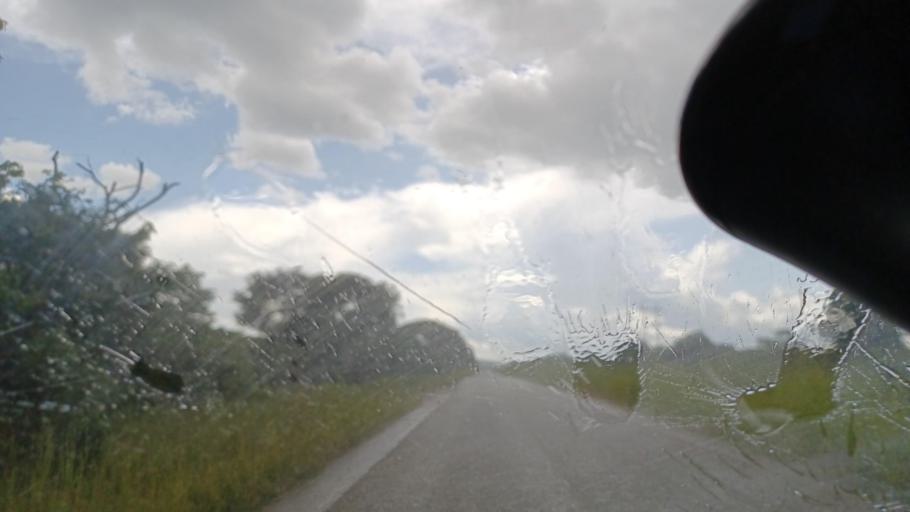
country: ZM
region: North-Western
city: Kasempa
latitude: -13.1014
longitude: 25.8926
